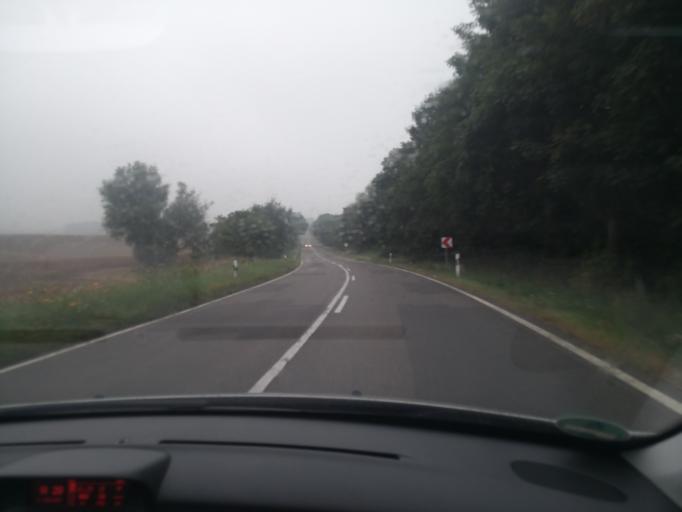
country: DE
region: Mecklenburg-Vorpommern
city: Woldegk
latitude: 53.4810
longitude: 13.6608
